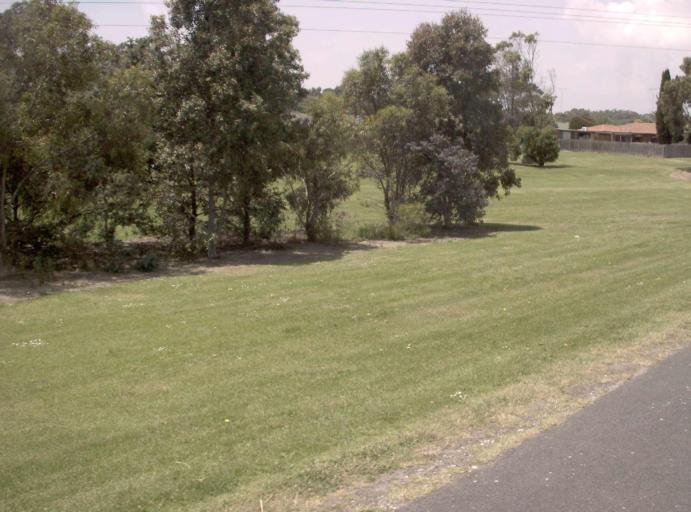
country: AU
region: Victoria
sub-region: Latrobe
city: Traralgon
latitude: -38.2095
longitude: 146.5450
